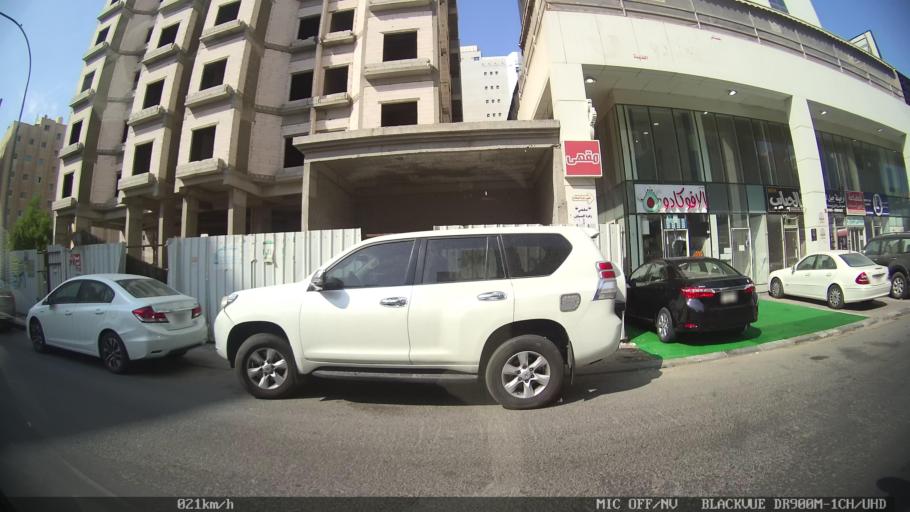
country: KW
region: Muhafazat Hawalli
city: Hawalli
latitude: 29.3416
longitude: 48.0184
